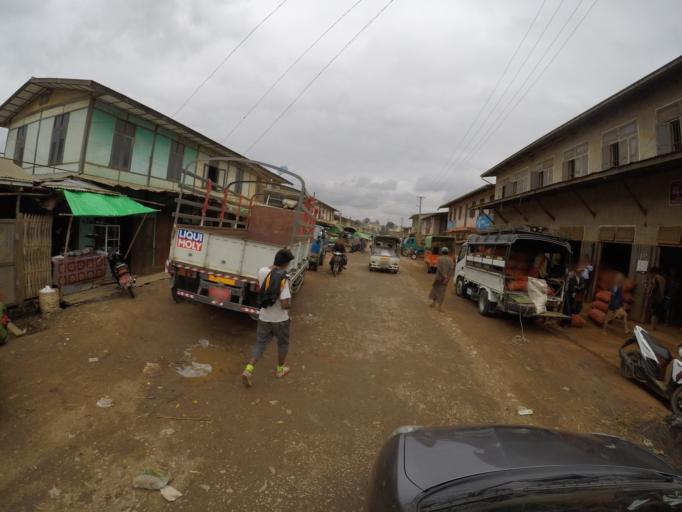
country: MM
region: Shan
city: Taunggyi
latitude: 20.6522
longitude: 96.6337
